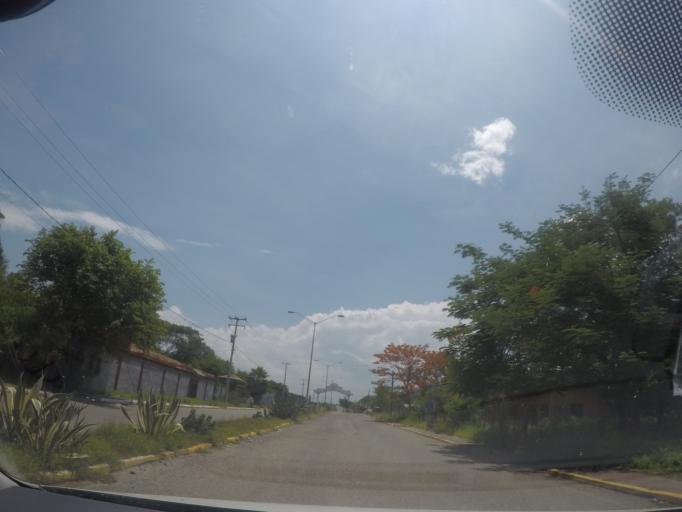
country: MX
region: Oaxaca
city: San Francisco Ixhuatan
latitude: 16.4027
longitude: -94.4537
